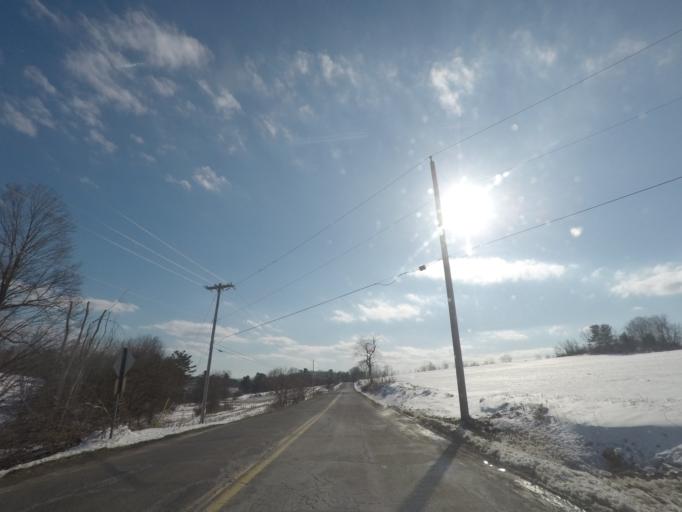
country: US
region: New York
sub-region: Rensselaer County
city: Hoosick Falls
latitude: 42.8649
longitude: -73.4937
